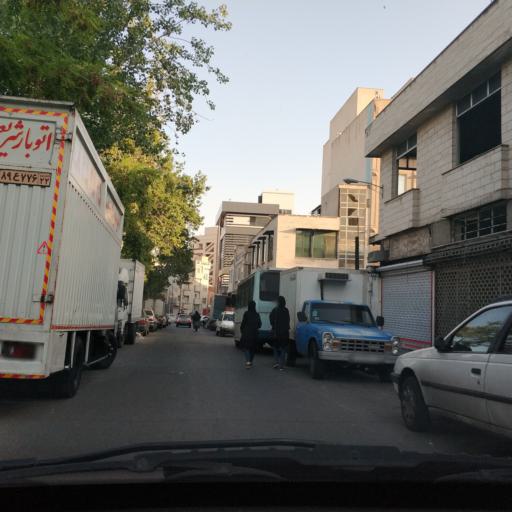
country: IR
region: Tehran
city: Tehran
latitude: 35.7178
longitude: 51.4772
